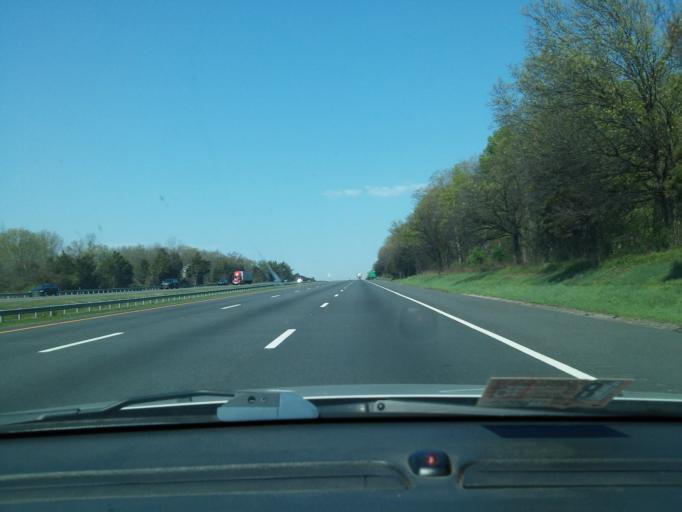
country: US
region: New Jersey
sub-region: Somerset County
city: Bedminster
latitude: 40.6432
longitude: -74.6894
